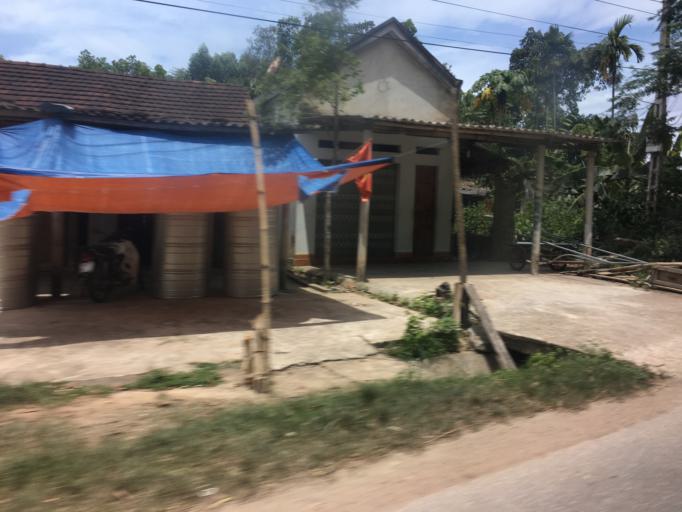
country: VN
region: Ha Tinh
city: Huong Khe
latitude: 18.2629
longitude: 105.6495
